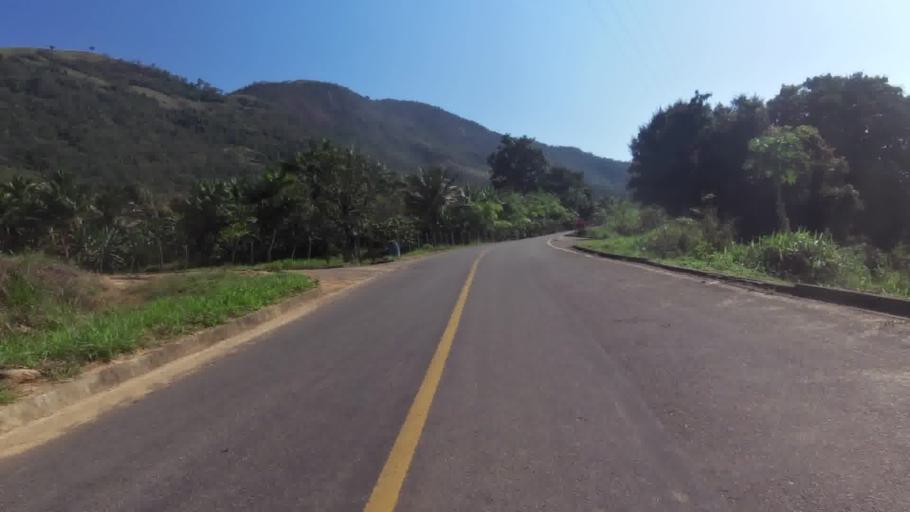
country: BR
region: Espirito Santo
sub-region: Alfredo Chaves
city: Alfredo Chaves
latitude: -20.6755
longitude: -40.7713
